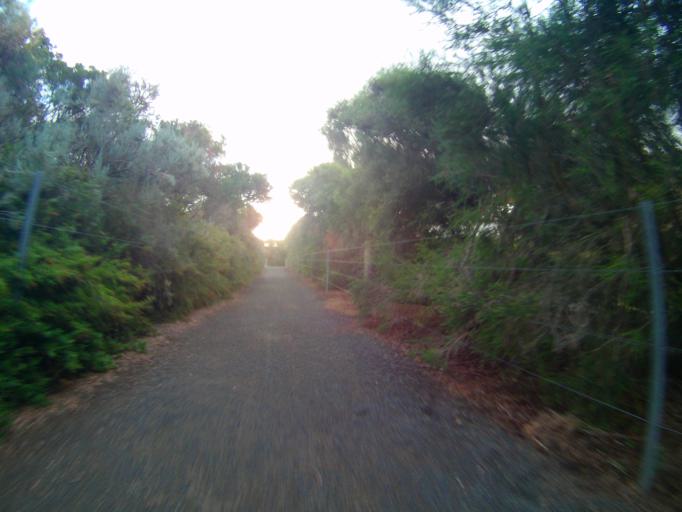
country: AU
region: Victoria
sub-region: Greater Geelong
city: Leopold
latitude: -38.2699
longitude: 144.5314
